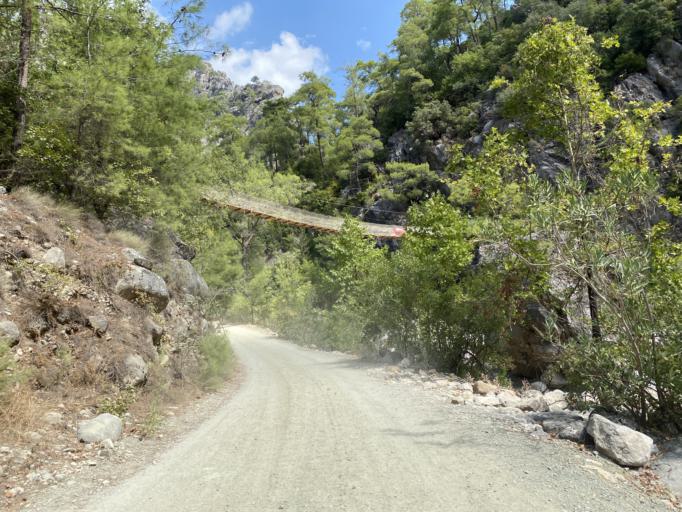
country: TR
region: Antalya
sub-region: Kemer
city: Goeynuek
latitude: 36.6814
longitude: 30.5278
